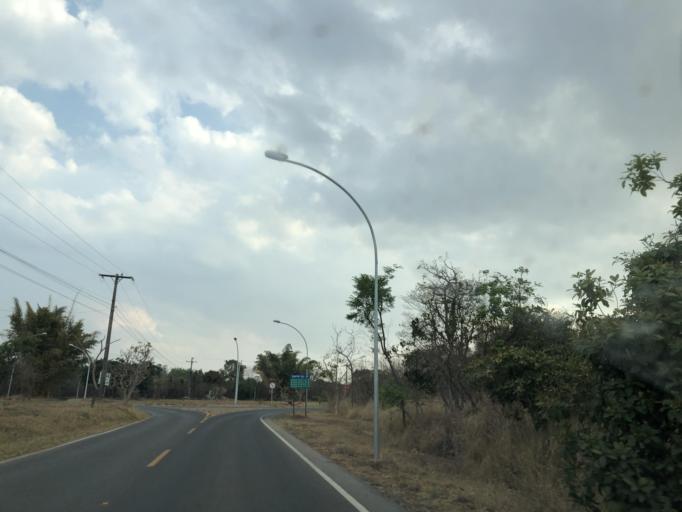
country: BR
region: Federal District
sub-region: Brasilia
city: Brasilia
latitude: -15.9378
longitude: -47.9748
